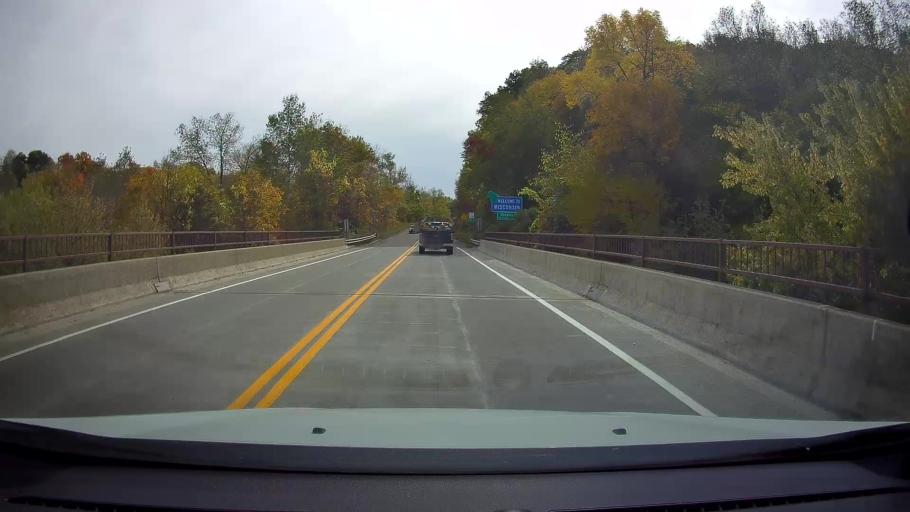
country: US
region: Wisconsin
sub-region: Polk County
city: Osceola
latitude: 45.3209
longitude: -92.7093
